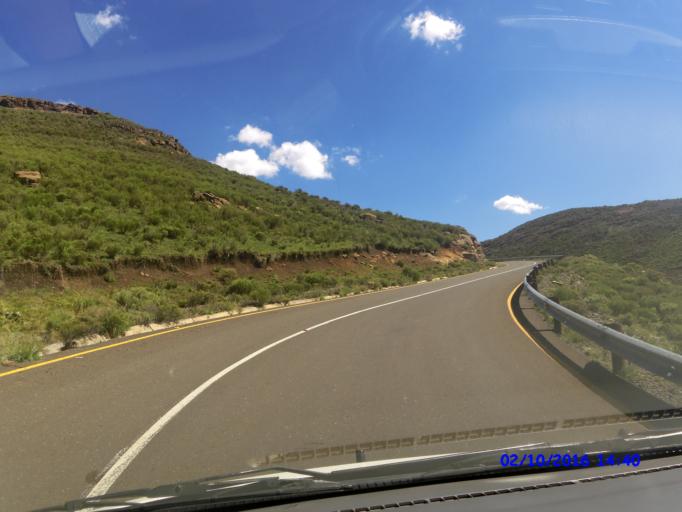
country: LS
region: Maseru
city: Nako
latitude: -29.5229
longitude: 28.0617
